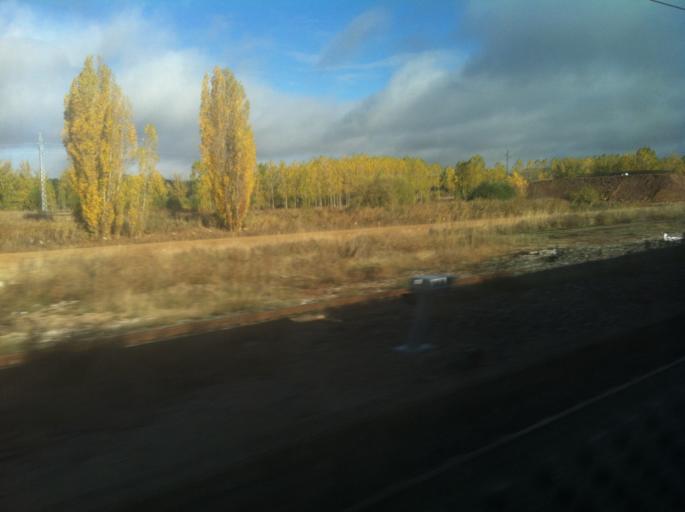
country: ES
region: Castille and Leon
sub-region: Provincia de Burgos
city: Buniel
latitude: 42.3275
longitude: -3.8114
